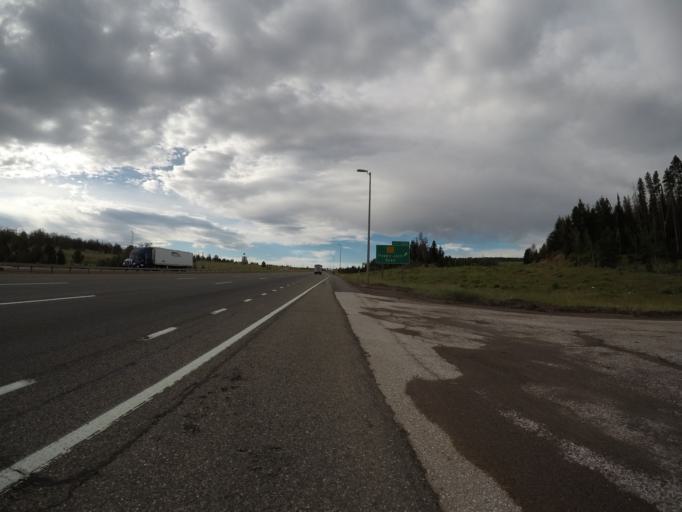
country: US
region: Wyoming
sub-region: Albany County
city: Laramie
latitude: 41.2465
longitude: -105.4421
